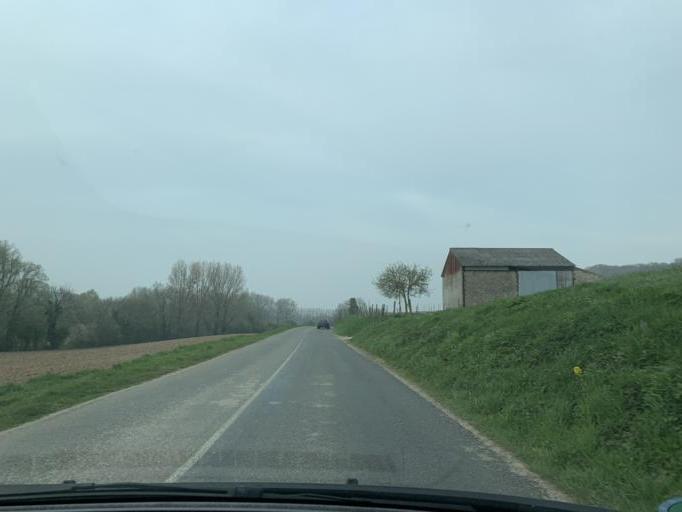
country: FR
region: Nord-Pas-de-Calais
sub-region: Departement du Pas-de-Calais
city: Montreuil
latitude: 50.4863
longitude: 1.7795
